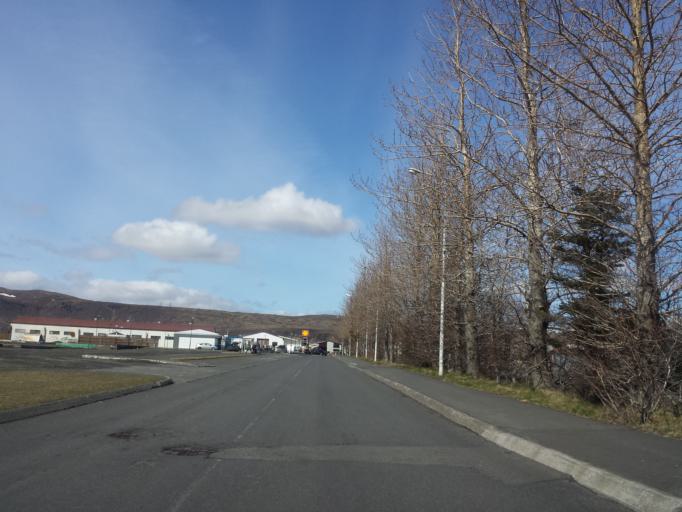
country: IS
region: South
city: Hveragerdi
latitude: 63.9949
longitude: -21.1825
